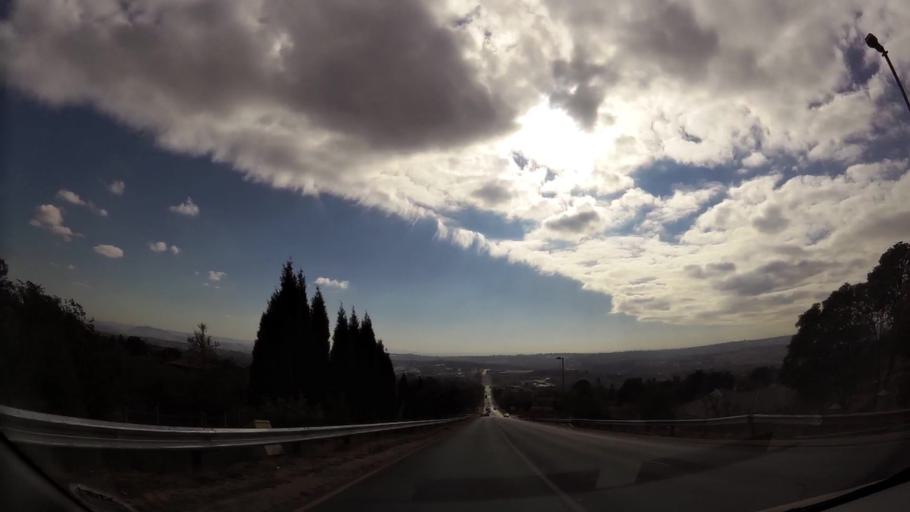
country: ZA
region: Gauteng
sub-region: City of Johannesburg Metropolitan Municipality
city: Roodepoort
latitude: -26.1009
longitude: 27.8639
